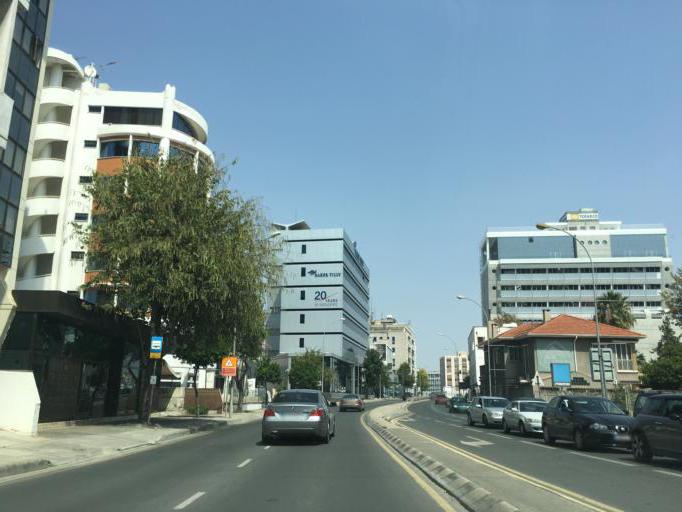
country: CY
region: Lefkosia
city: Nicosia
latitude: 35.1636
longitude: 33.3545
